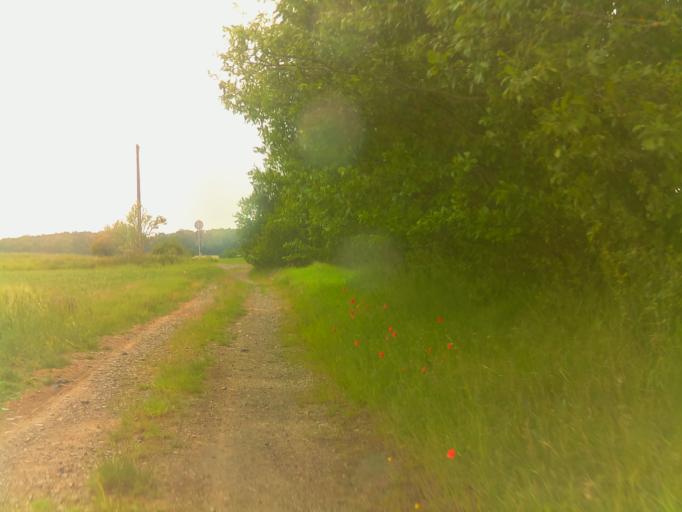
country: DE
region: Thuringia
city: Henneberg
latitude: 50.4533
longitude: 10.3679
